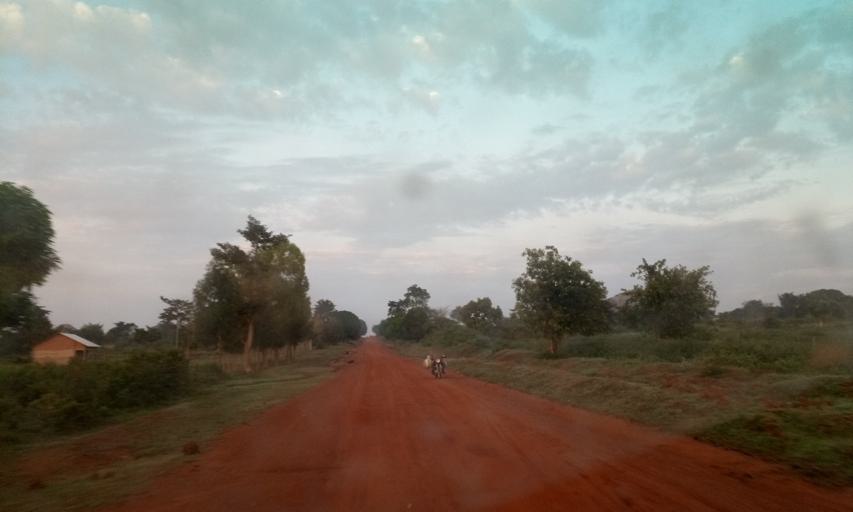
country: UG
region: Eastern Region
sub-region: Ngora District
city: Ngora
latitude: 1.4669
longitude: 33.8098
